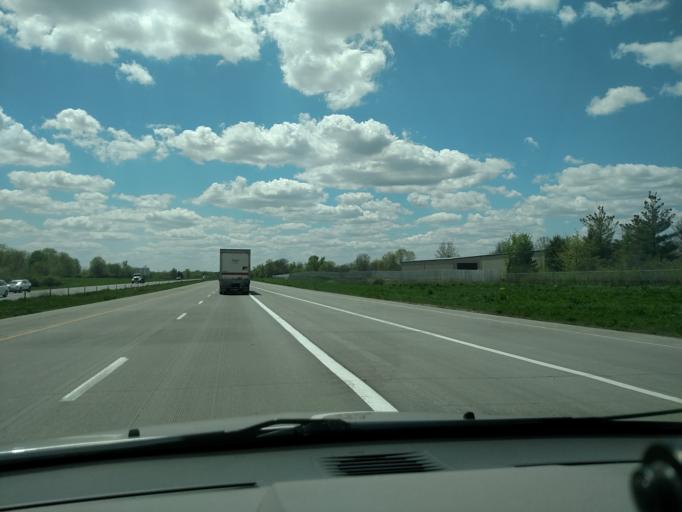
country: US
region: Iowa
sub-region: Polk County
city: Ankeny
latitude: 41.7555
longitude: -93.5715
